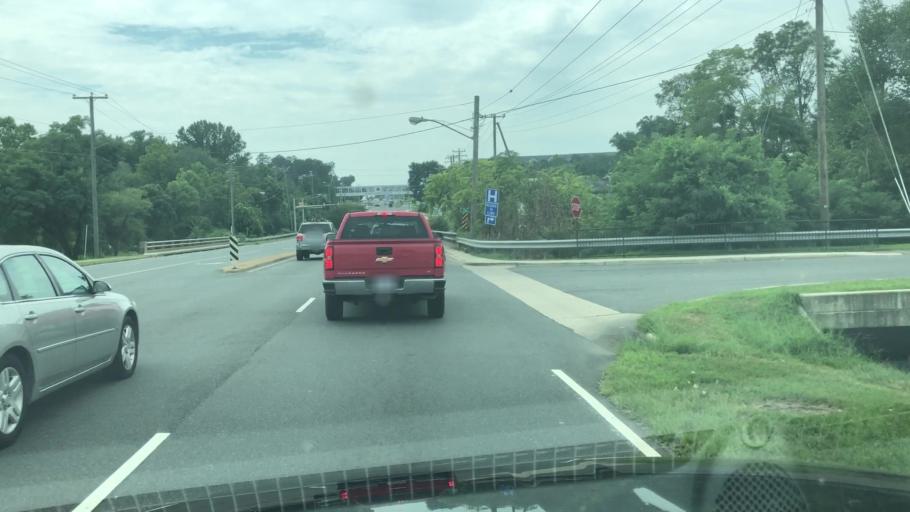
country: US
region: Virginia
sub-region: Stafford County
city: Falmouth
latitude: 38.3120
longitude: -77.4763
